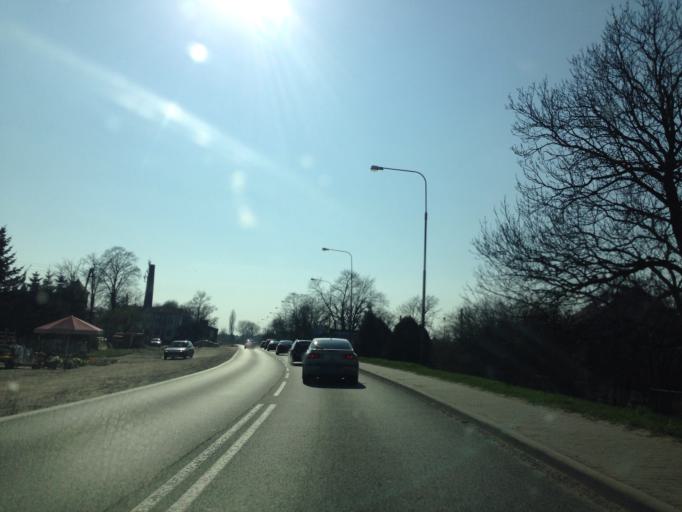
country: PL
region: Lower Silesian Voivodeship
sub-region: Powiat olesnicki
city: Olesnica
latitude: 51.2019
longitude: 17.3230
